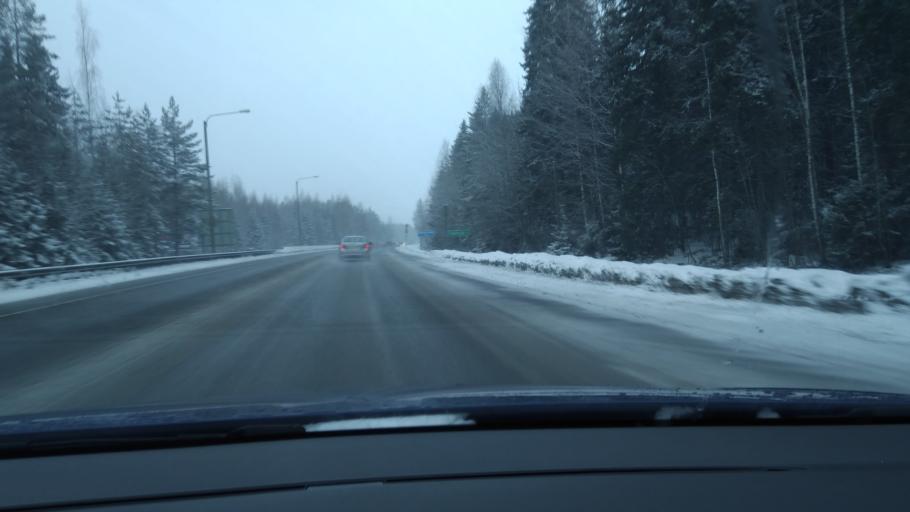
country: FI
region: Pirkanmaa
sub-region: Tampere
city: Kangasala
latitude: 61.5295
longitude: 23.9443
